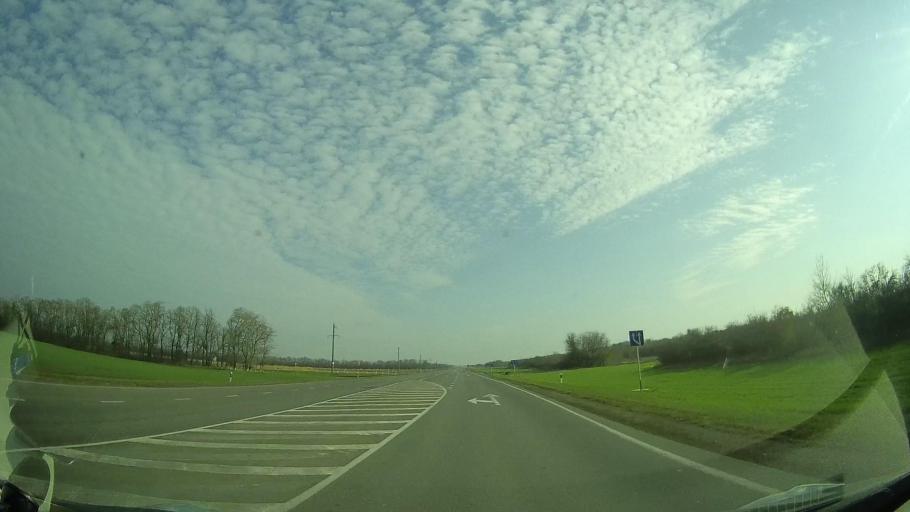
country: RU
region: Rostov
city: Gigant
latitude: 46.5247
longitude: 41.2542
